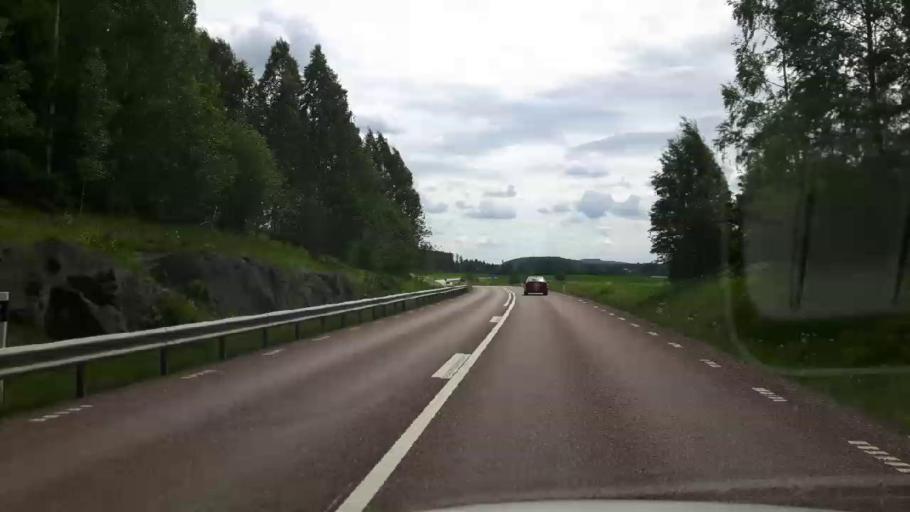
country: SE
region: Dalarna
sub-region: Hedemora Kommun
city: Hedemora
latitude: 60.3345
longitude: 15.9453
